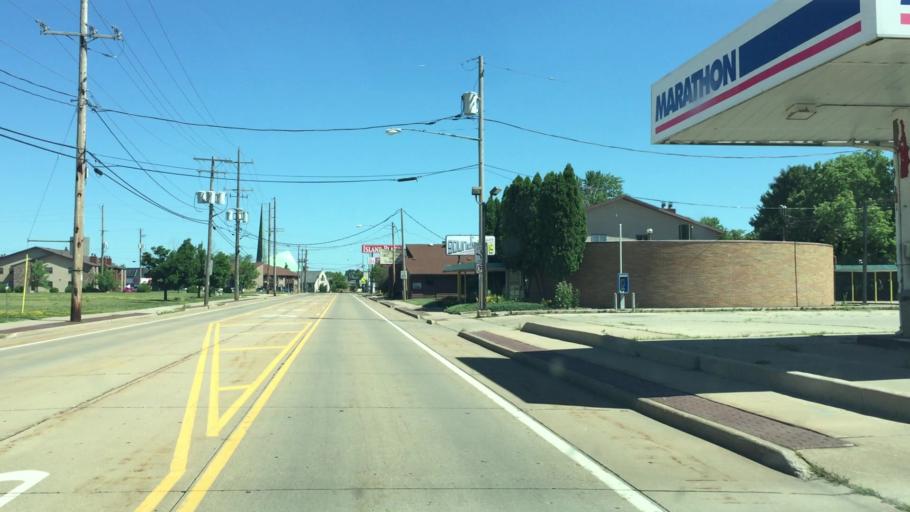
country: US
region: Wisconsin
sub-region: Winnebago County
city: Neenah
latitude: 44.1905
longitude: -88.4547
